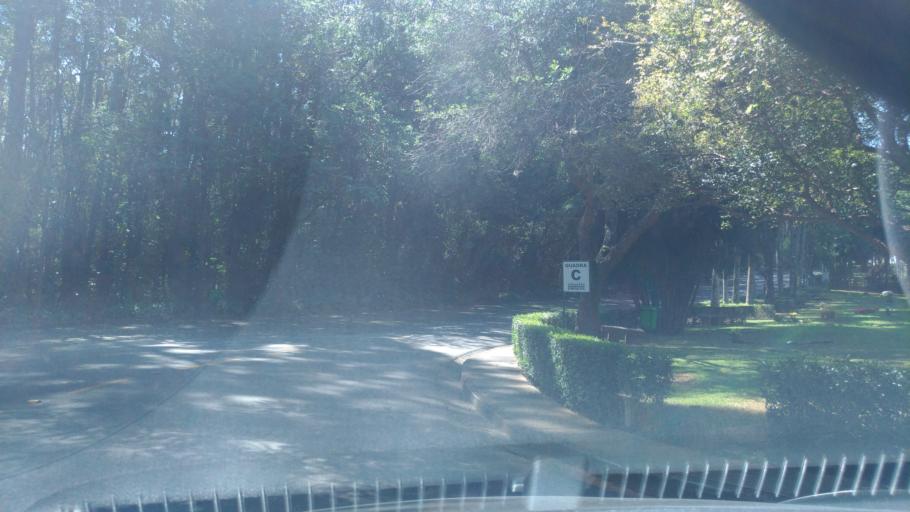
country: BR
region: Sao Paulo
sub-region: Osasco
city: Osasco
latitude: -23.4432
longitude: -46.7847
